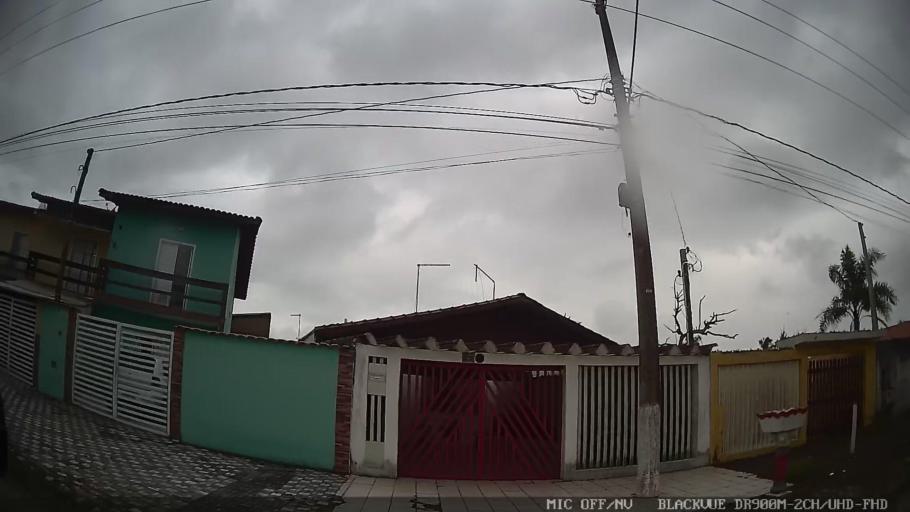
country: BR
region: Sao Paulo
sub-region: Itanhaem
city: Itanhaem
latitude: -24.1399
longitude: -46.7076
